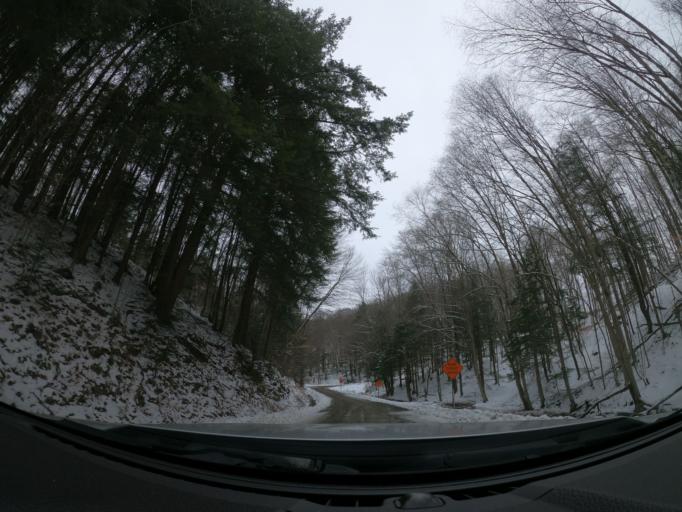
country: US
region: New York
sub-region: Cortland County
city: Homer
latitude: 42.7290
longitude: -76.2805
